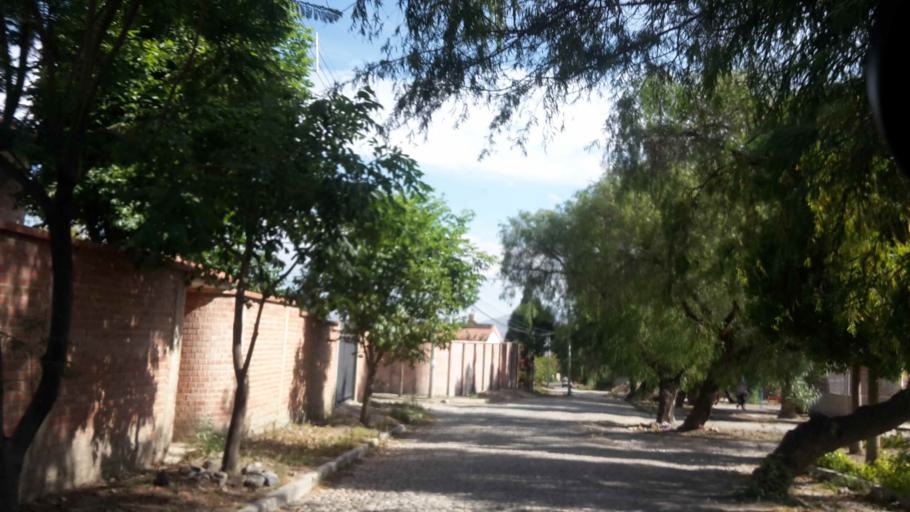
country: BO
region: Cochabamba
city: Cochabamba
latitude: -17.3494
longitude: -66.1977
